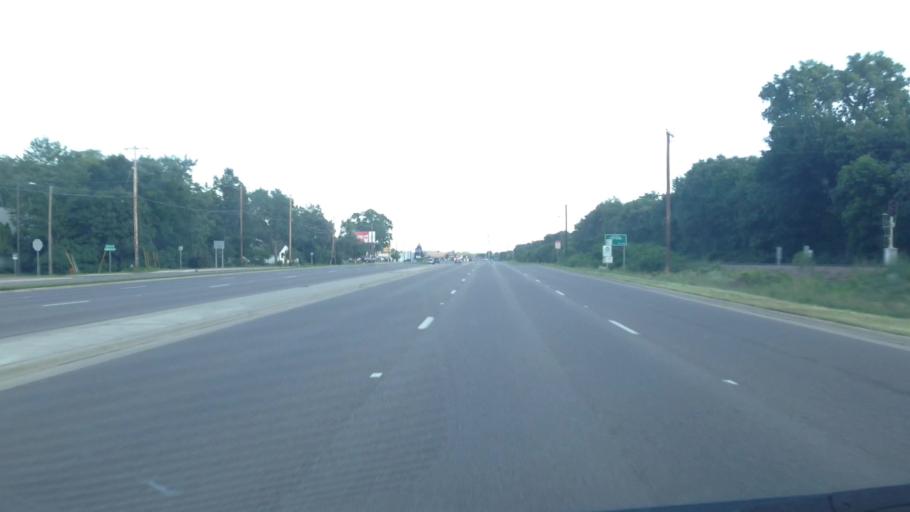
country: US
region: Minnesota
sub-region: Hennepin County
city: Brooklyn Park
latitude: 45.0662
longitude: -93.3661
